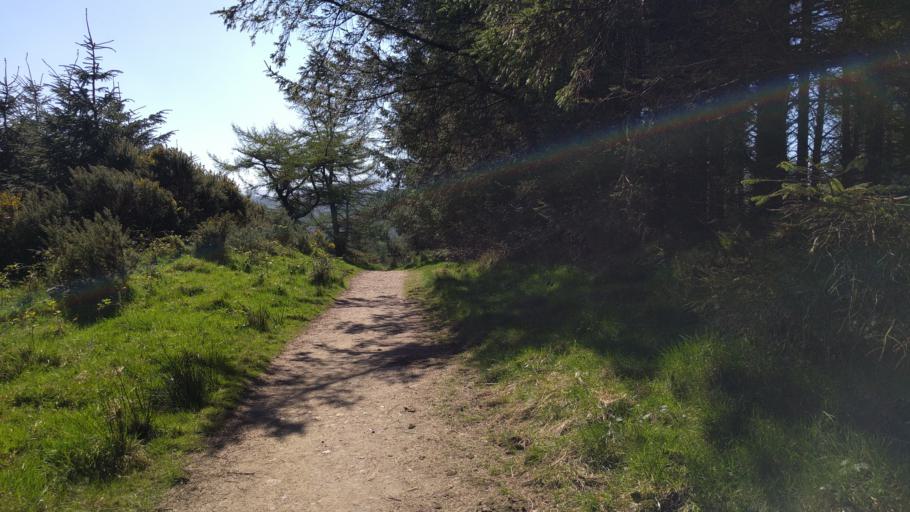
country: IE
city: Knocklyon
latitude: 53.2511
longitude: -6.3285
